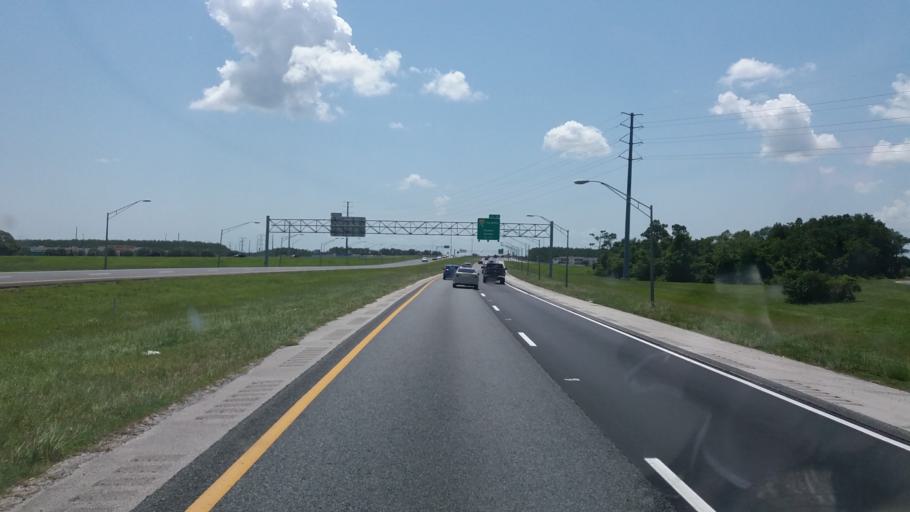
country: US
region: Florida
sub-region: Orange County
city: Hunters Creek
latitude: 28.3747
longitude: -81.4102
